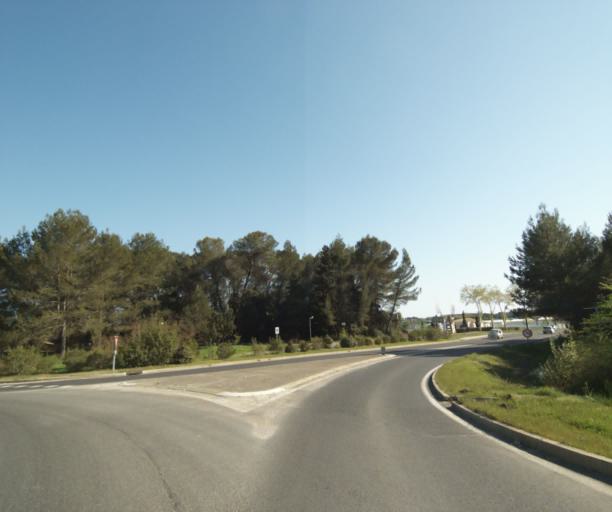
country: FR
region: Languedoc-Roussillon
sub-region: Departement de l'Herault
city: Jacou
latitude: 43.6715
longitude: 3.9128
